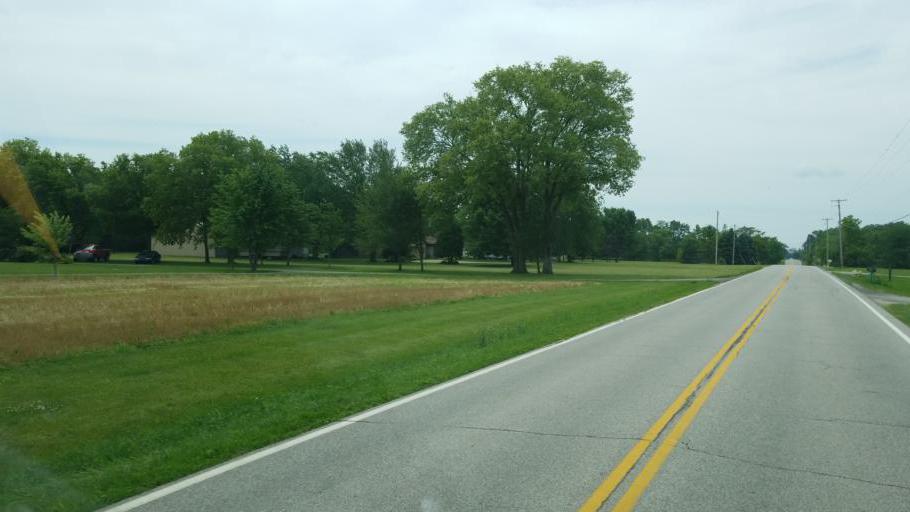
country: US
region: Ohio
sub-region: Madison County
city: Plain City
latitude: 40.0549
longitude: -83.2586
